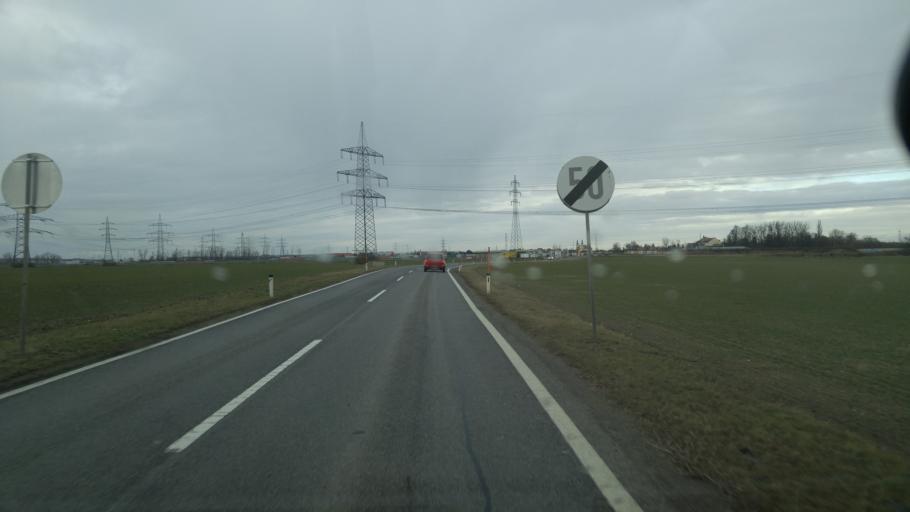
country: AT
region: Lower Austria
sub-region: Politischer Bezirk Modling
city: Achau
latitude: 48.0876
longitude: 16.4069
